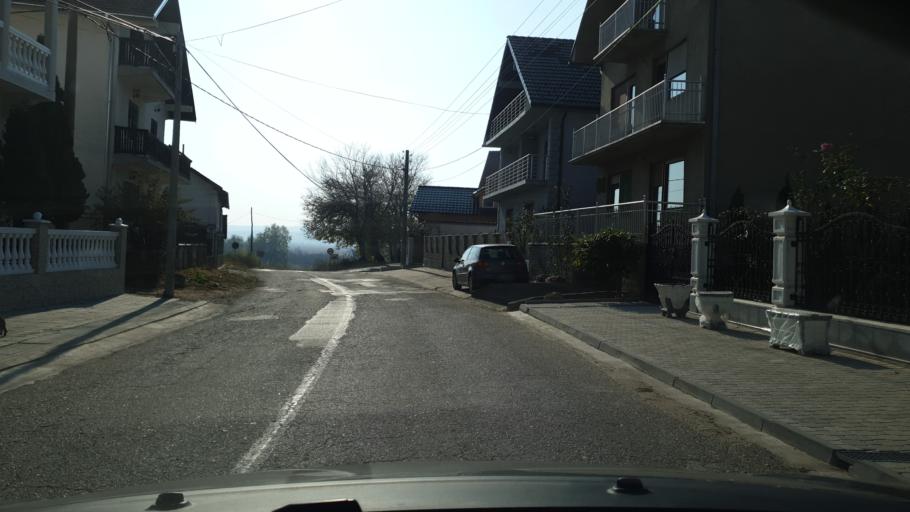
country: BG
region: Vidin
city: Bregovo
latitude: 44.1928
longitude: 22.5948
